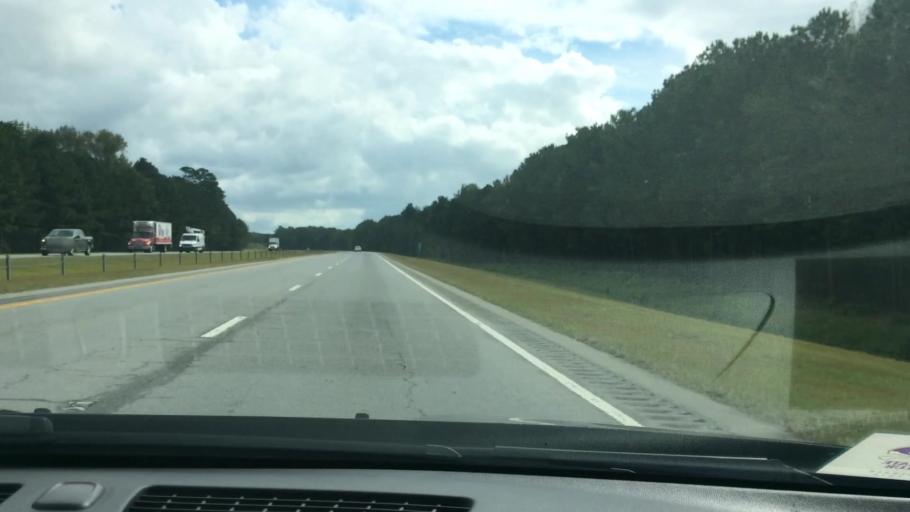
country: US
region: North Carolina
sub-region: Pitt County
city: Farmville
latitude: 35.6286
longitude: -77.7155
